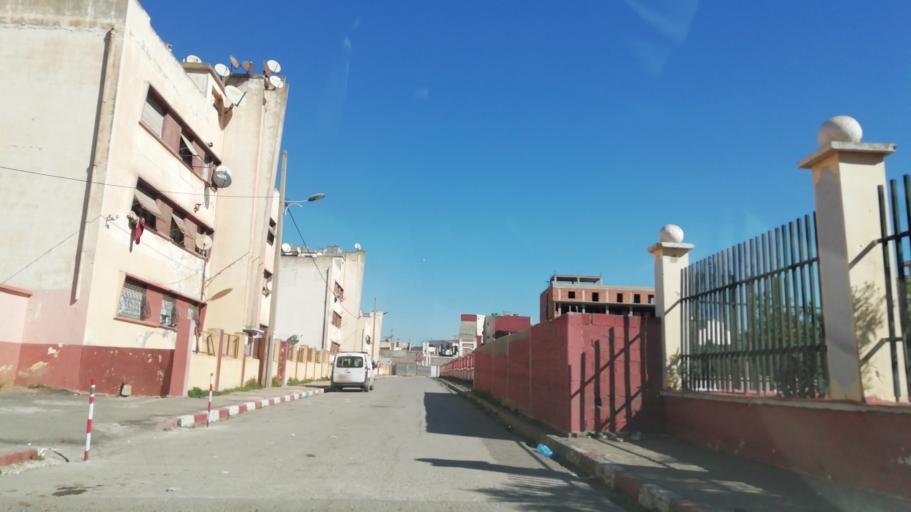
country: DZ
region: Oran
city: Oran
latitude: 35.6936
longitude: -0.6139
